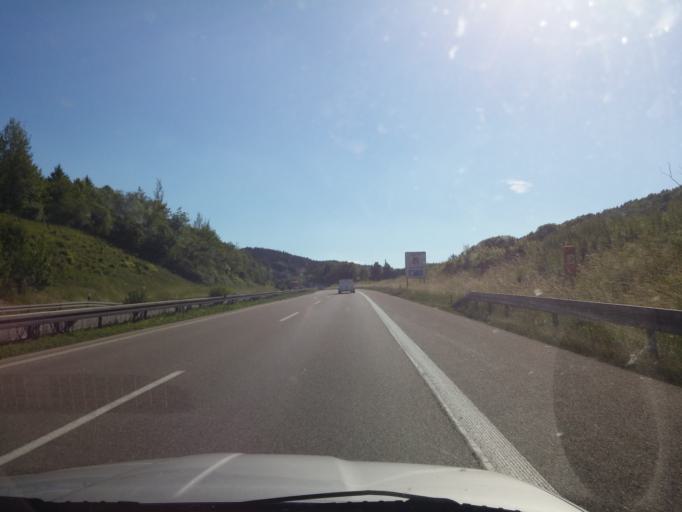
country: DE
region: Baden-Wuerttemberg
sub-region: Tuebingen Region
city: Aichstetten
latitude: 47.8974
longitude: 10.0541
